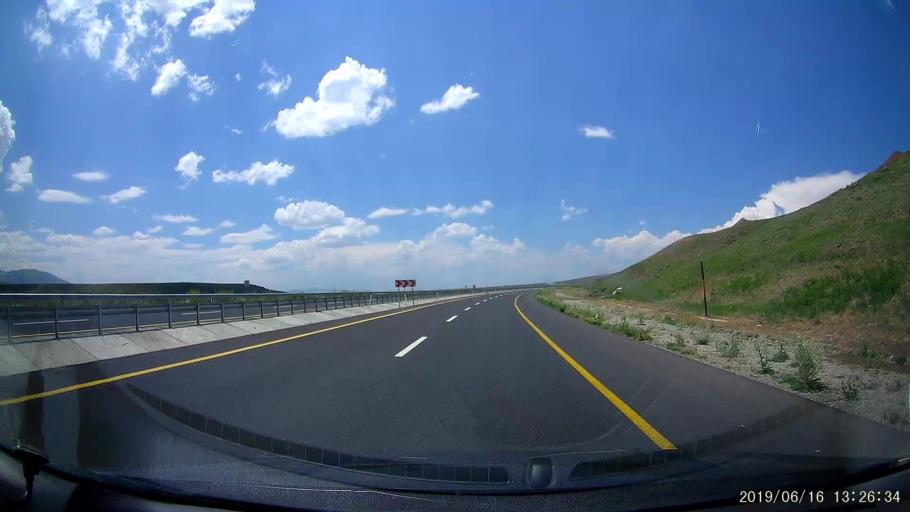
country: TR
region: Agri
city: Taslicay
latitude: 39.6597
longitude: 43.3251
